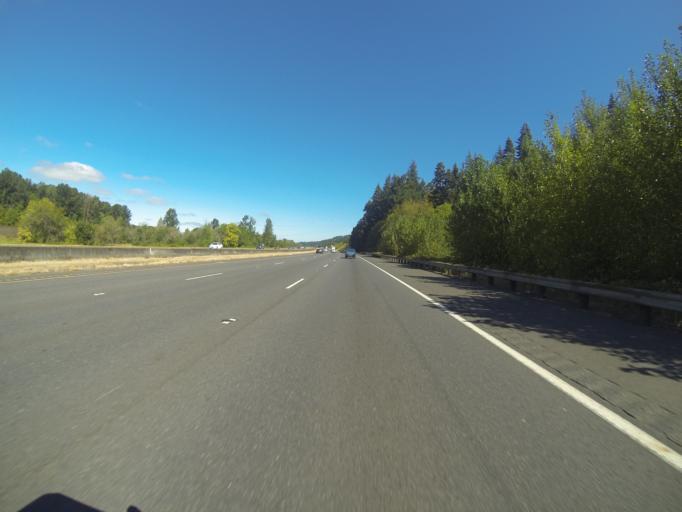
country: US
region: Oregon
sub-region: Columbia County
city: Rainier
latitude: 46.0811
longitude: -122.8666
